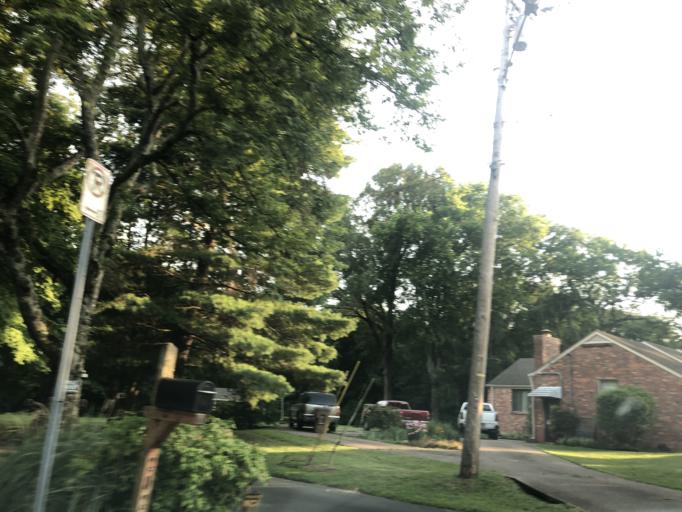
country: US
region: Tennessee
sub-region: Davidson County
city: Nashville
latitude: 36.1581
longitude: -86.6999
